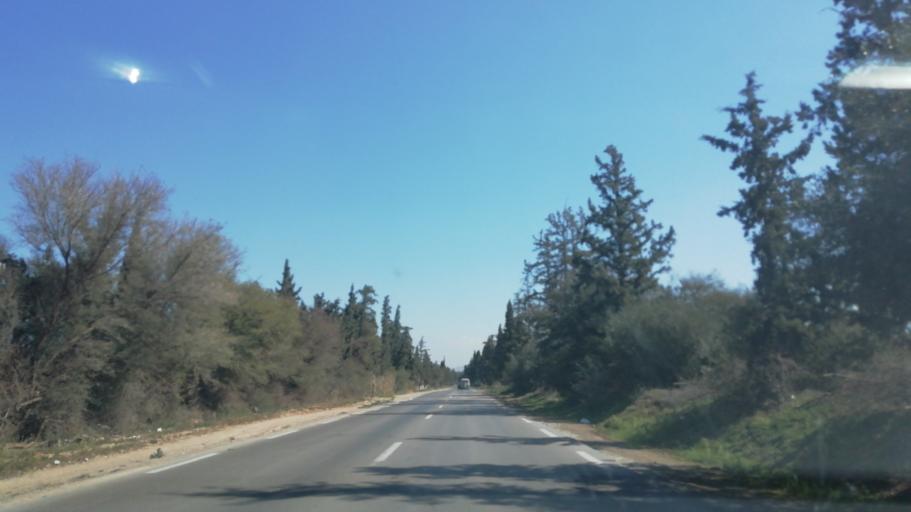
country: DZ
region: Mascara
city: Sig
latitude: 35.5721
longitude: -0.0254
